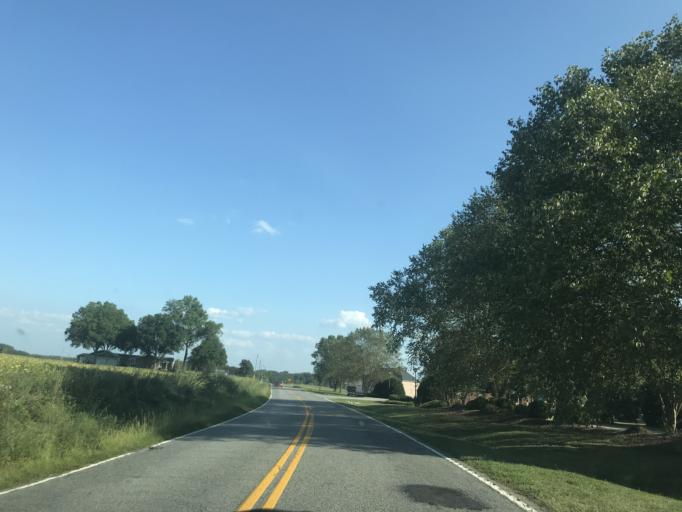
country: US
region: South Carolina
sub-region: Cherokee County
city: Gaffney
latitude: 35.1265
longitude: -81.6883
